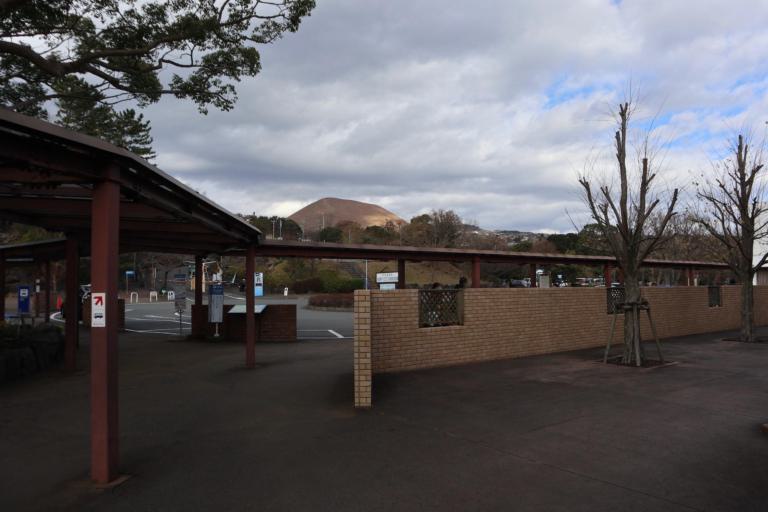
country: JP
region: Shizuoka
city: Ito
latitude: 34.8787
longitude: 139.1087
